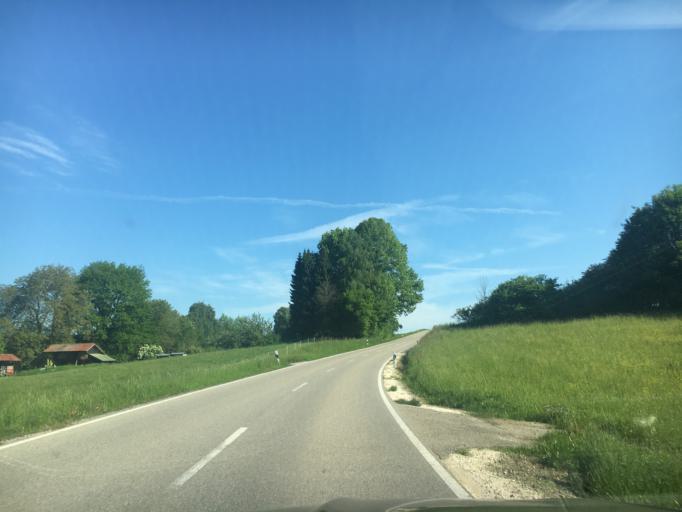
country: DE
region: Bavaria
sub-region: Upper Bavaria
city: Garching an der Alz
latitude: 48.1181
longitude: 12.5954
